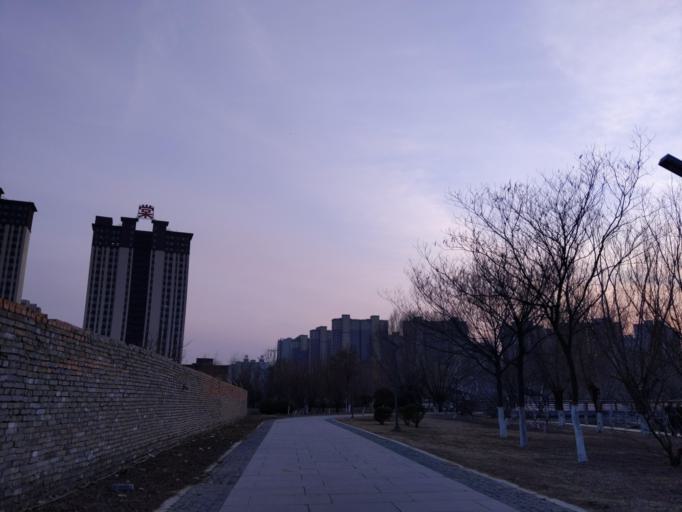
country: CN
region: Henan Sheng
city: Zhongyuanlu
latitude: 35.7760
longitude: 115.1280
